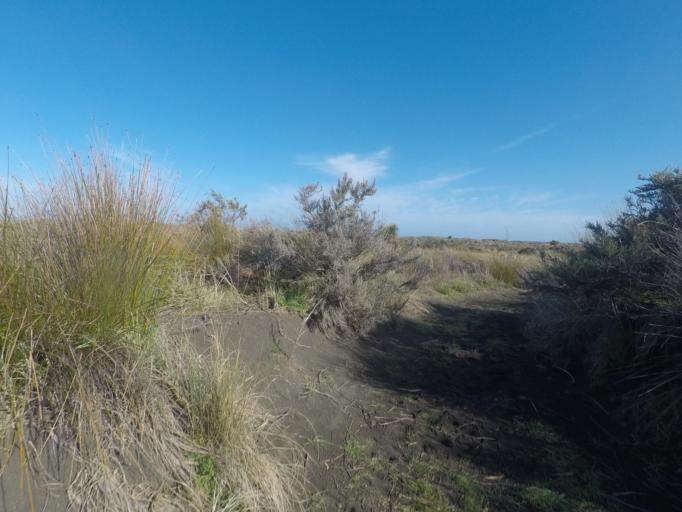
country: NZ
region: Auckland
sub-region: Auckland
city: Titirangi
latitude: -37.0087
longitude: 174.4808
